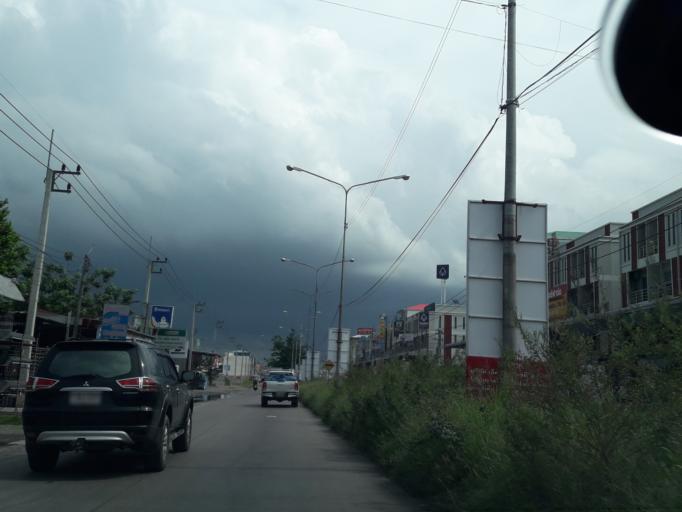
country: TH
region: Pathum Thani
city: Khlong Luang
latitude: 14.0780
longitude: 100.6339
